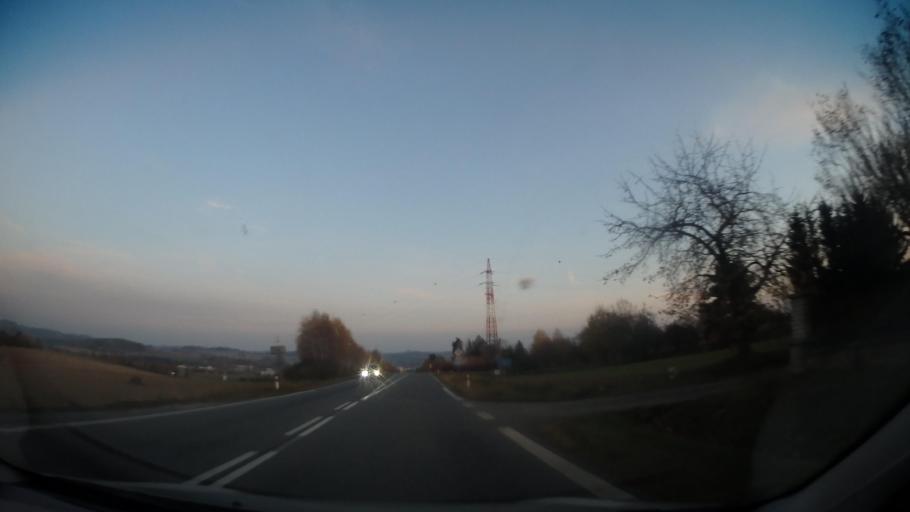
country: CZ
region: Vysocina
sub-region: Okres Pelhrimov
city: Pelhrimov
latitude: 49.4419
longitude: 15.2036
